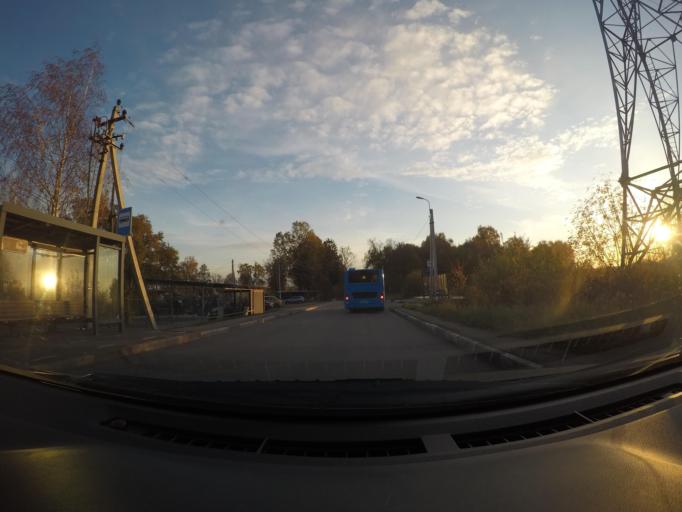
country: RU
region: Moskovskaya
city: Firsanovka
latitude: 55.9384
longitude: 37.2491
